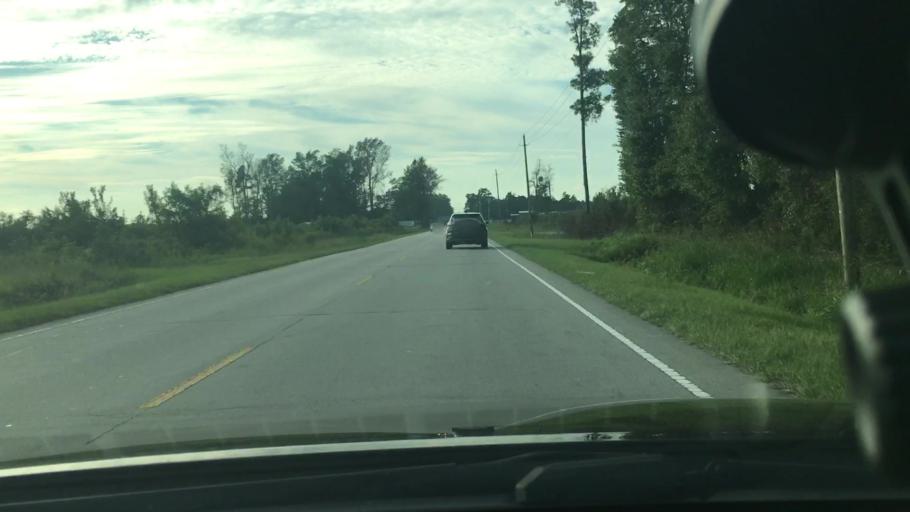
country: US
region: North Carolina
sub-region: Pitt County
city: Windsor
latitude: 35.4720
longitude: -77.2868
